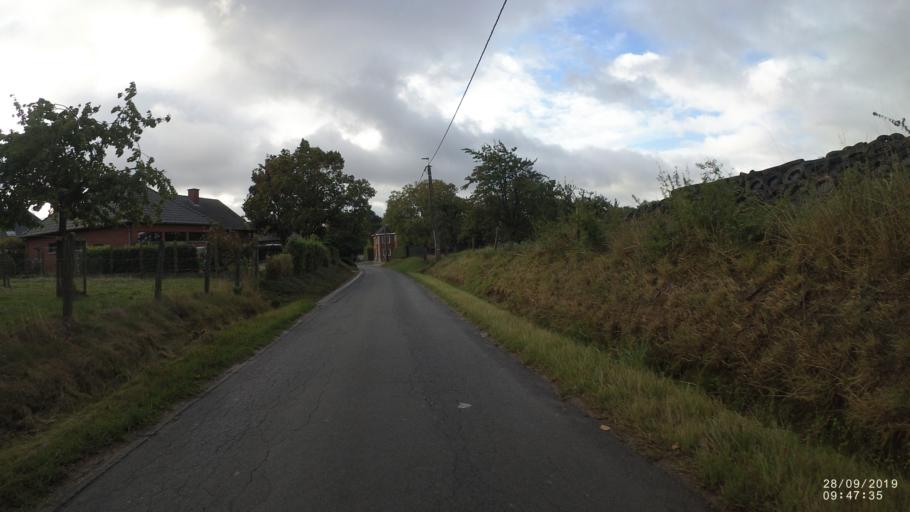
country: BE
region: Wallonia
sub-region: Province du Hainaut
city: Flobecq
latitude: 50.8014
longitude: 3.7433
